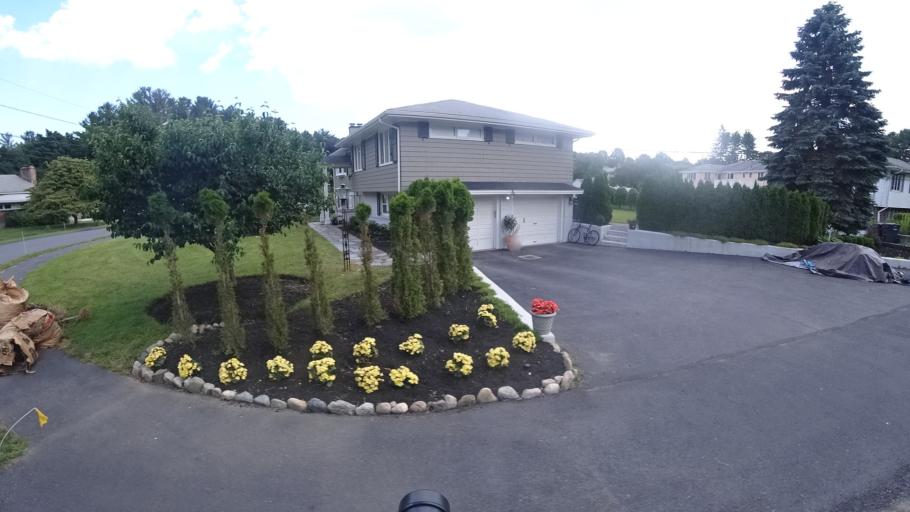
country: US
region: Massachusetts
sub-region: Norfolk County
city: Dedham
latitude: 42.2723
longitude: -71.1850
